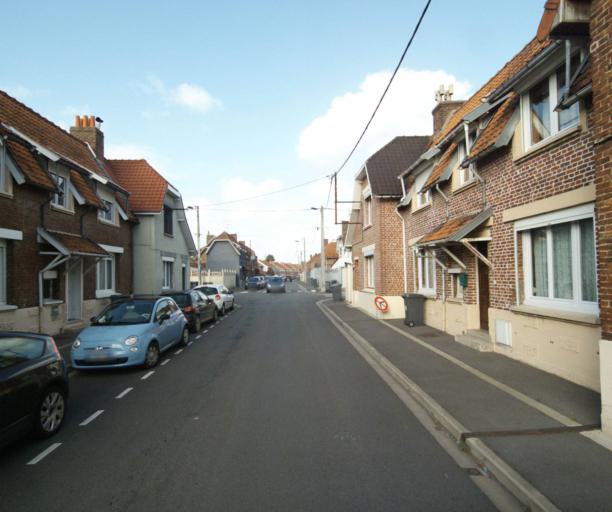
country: FR
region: Nord-Pas-de-Calais
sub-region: Departement du Nord
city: La Bassee
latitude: 50.5338
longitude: 2.8054
